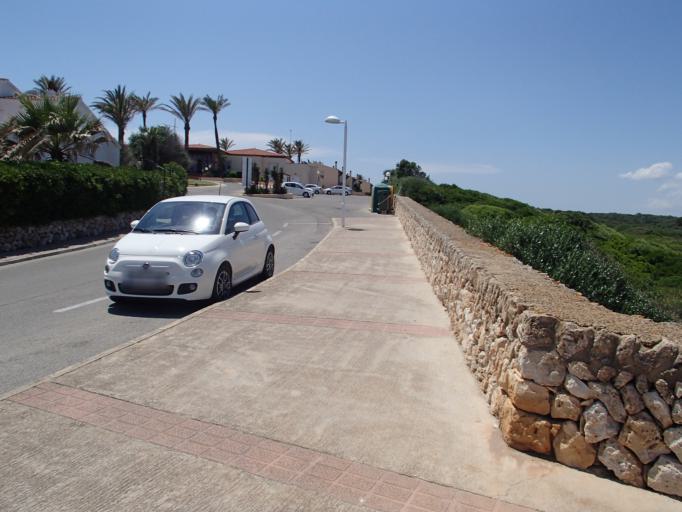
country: ES
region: Balearic Islands
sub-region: Illes Balears
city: Es Castell
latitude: 39.8399
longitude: 4.2999
